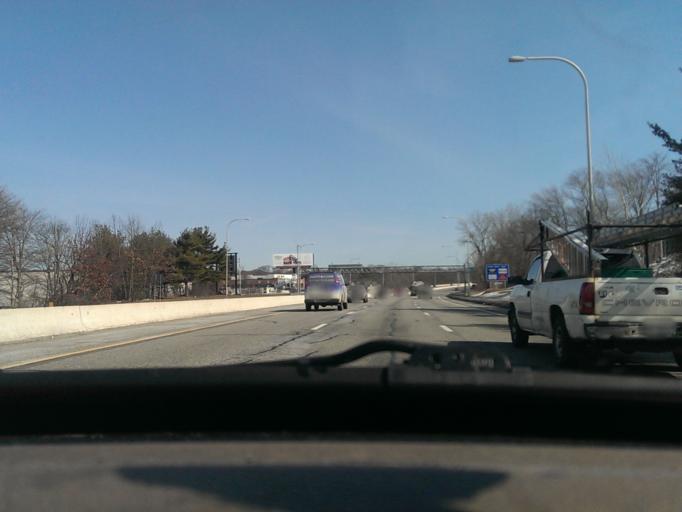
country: US
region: Massachusetts
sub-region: Bristol County
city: Seekonk
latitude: 41.8099
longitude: -71.3477
